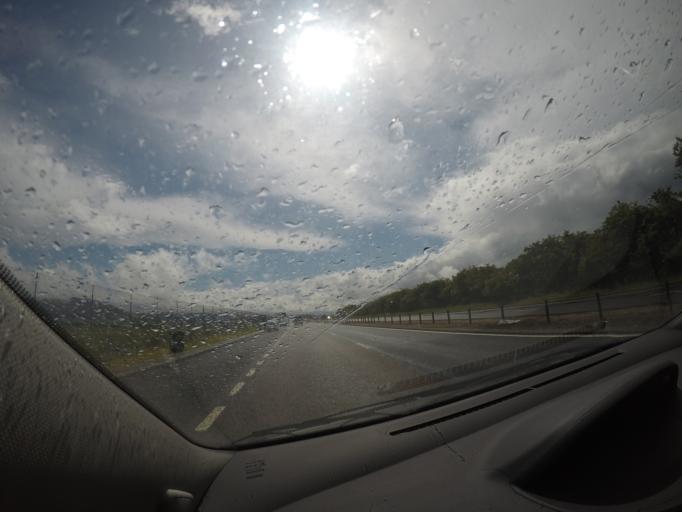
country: GB
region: Scotland
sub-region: Perth and Kinross
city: Auchterarder
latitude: 56.3277
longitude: -3.6402
